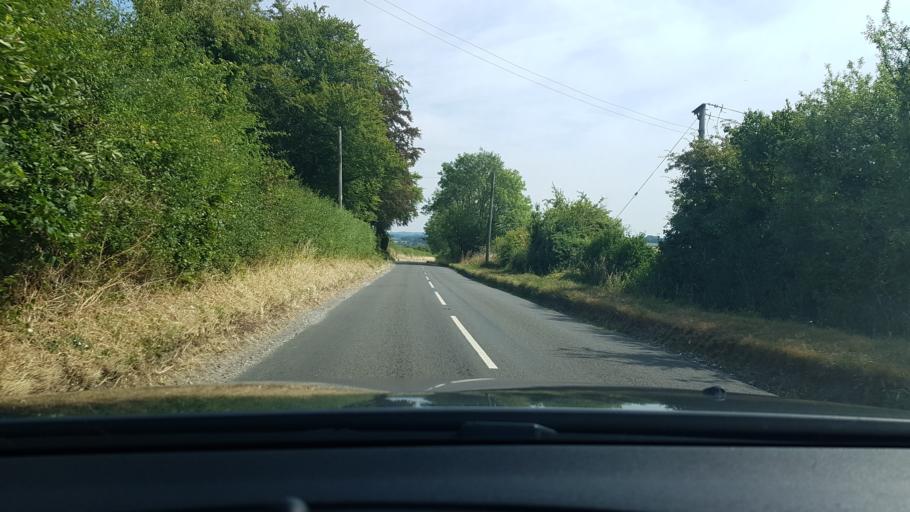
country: GB
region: England
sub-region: Wiltshire
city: Shalbourne
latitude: 51.3702
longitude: -1.5539
